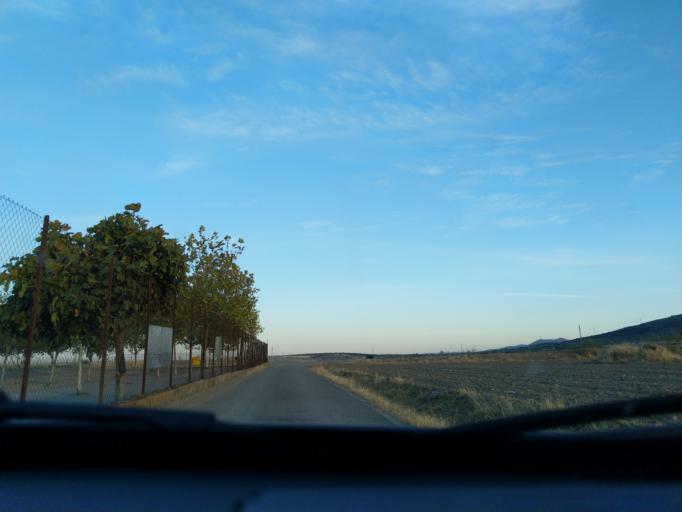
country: ES
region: Extremadura
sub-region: Provincia de Badajoz
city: Casas de Reina
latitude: 38.2013
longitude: -5.9529
